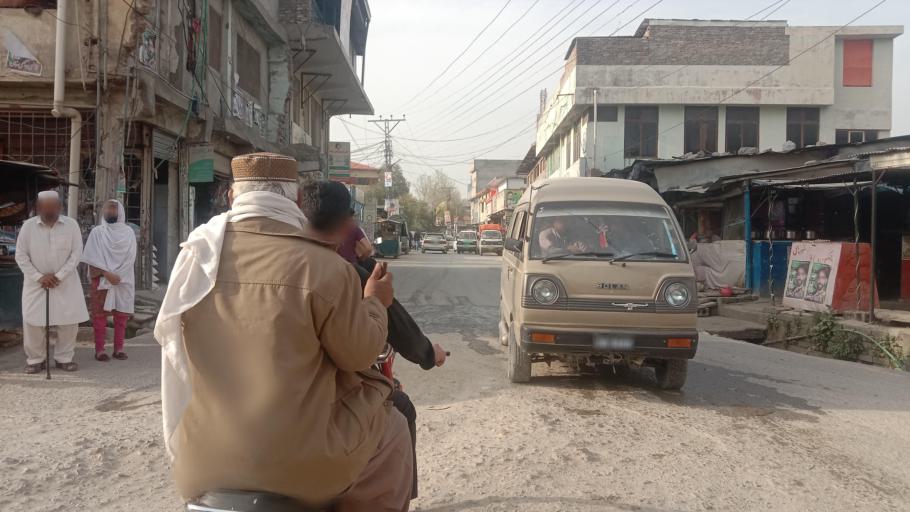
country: PK
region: Khyber Pakhtunkhwa
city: Abbottabad
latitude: 34.1584
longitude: 73.2643
